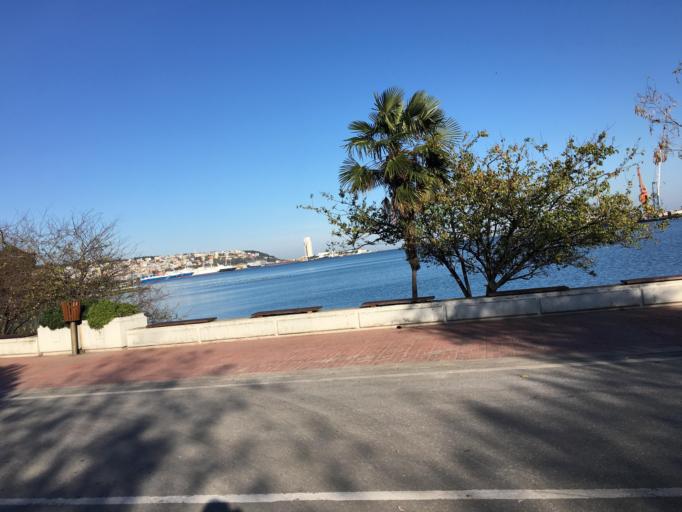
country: TR
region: Samsun
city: Samsun
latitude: 41.2865
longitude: 36.3454
